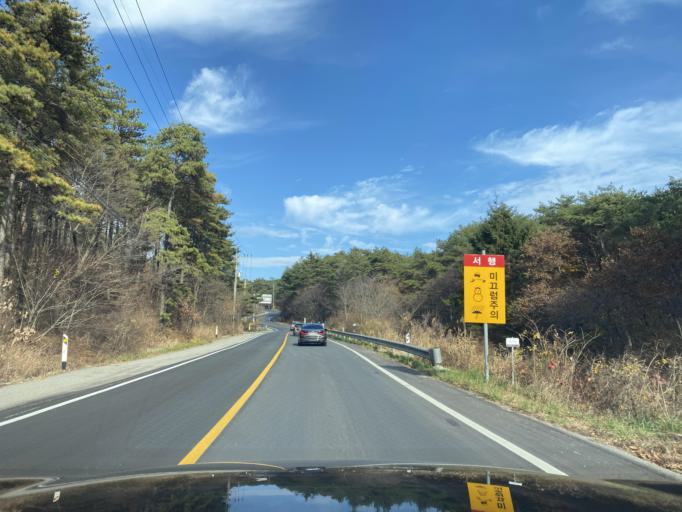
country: KR
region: Chungcheongnam-do
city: Hongsung
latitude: 36.6580
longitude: 126.6270
